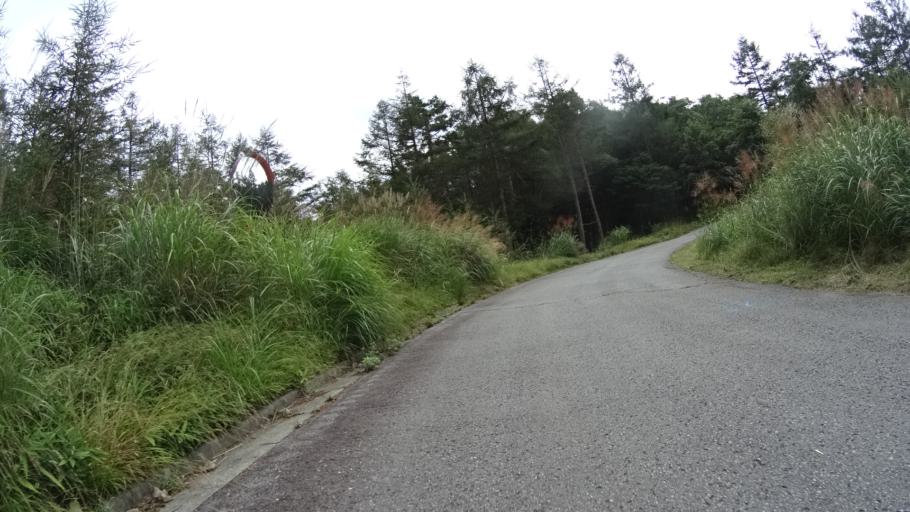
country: JP
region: Yamanashi
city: Kofu-shi
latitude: 35.8246
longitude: 138.5551
